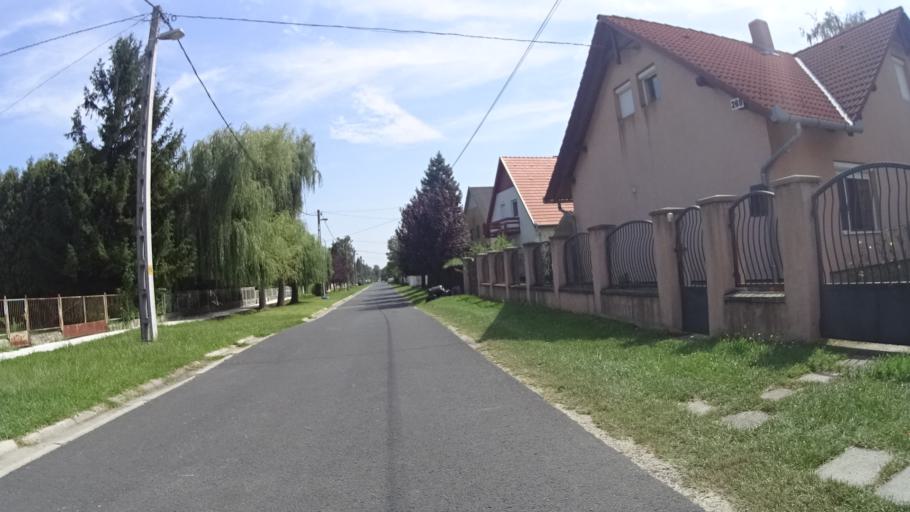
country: HU
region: Somogy
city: Kethely
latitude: 46.7032
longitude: 17.4024
